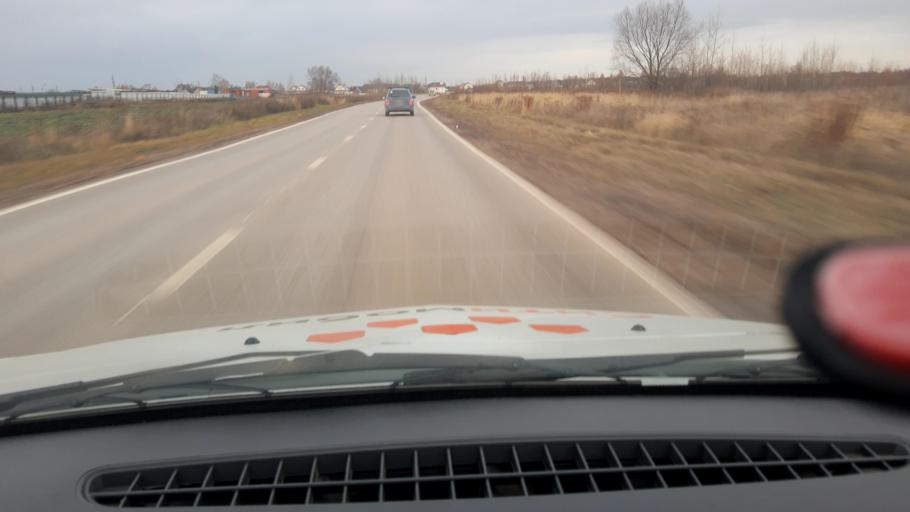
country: RU
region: Bashkortostan
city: Kabakovo
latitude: 54.7407
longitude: 56.2026
